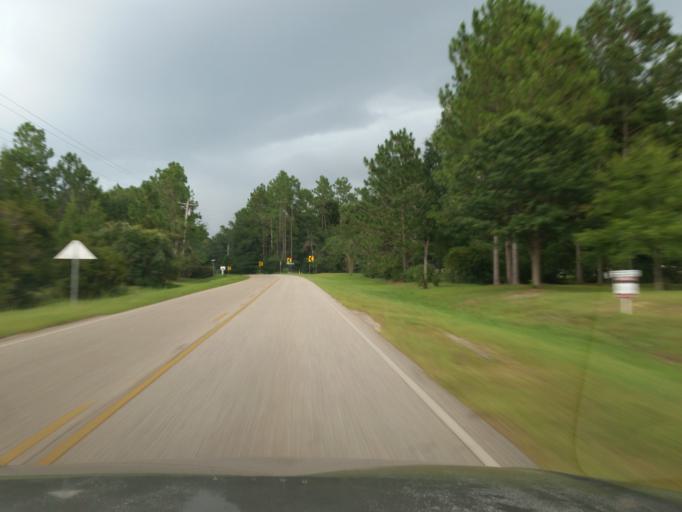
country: US
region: Alabama
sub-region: Baldwin County
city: Robertsdale
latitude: 30.5782
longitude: -87.5725
